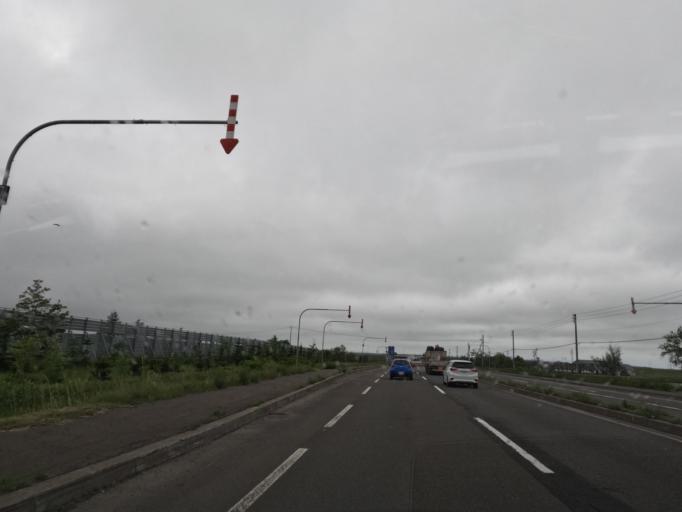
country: JP
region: Hokkaido
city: Tobetsu
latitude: 43.1791
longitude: 141.5226
